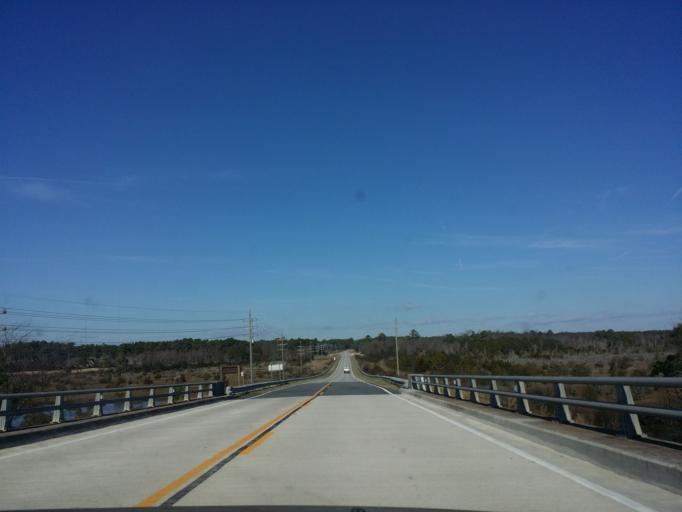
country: US
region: North Carolina
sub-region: Onslow County
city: Sneads Ferry
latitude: 34.5029
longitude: -77.4307
